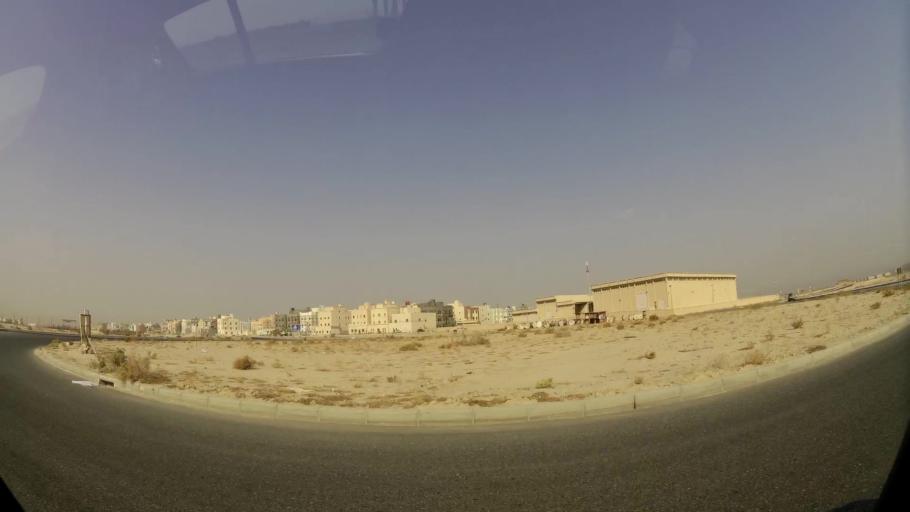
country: KW
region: Muhafazat al Jahra'
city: Al Jahra'
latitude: 29.3472
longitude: 47.7812
